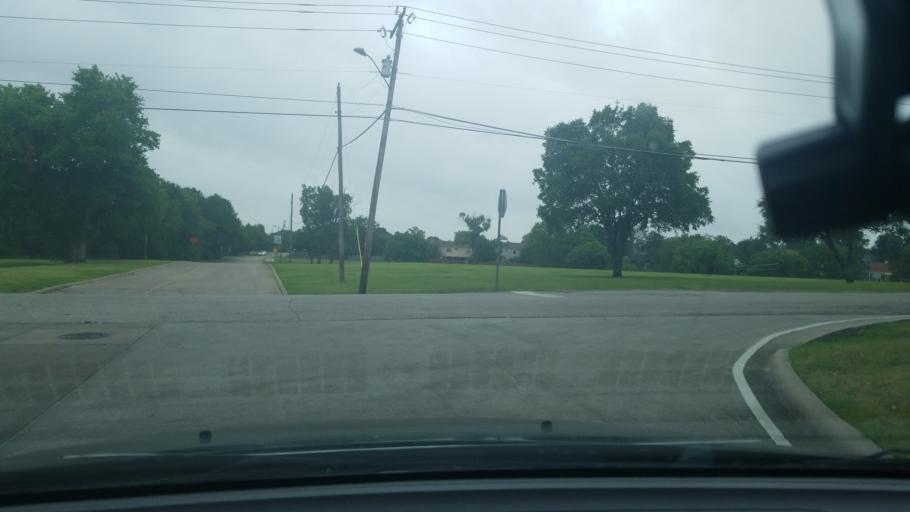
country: US
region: Texas
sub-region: Dallas County
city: Mesquite
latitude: 32.7916
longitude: -96.6491
